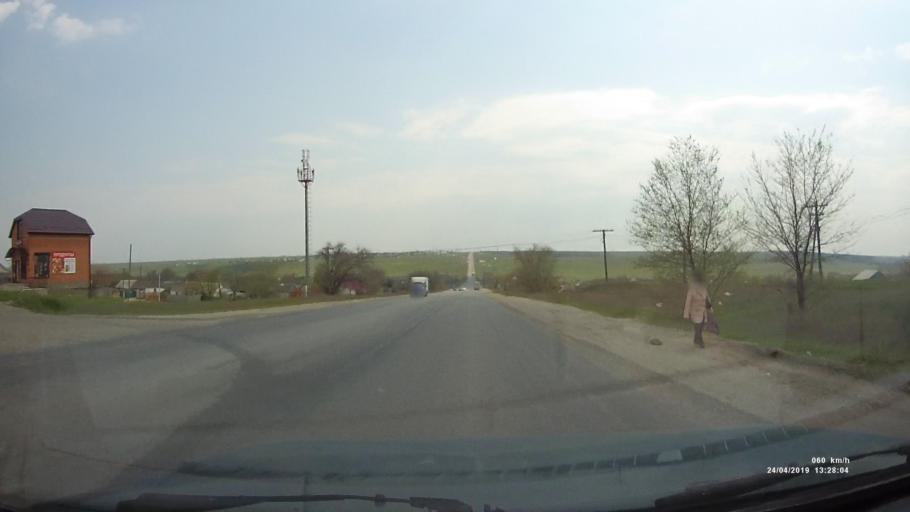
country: RU
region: Kalmykiya
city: Arshan'
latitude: 46.2758
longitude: 44.2285
